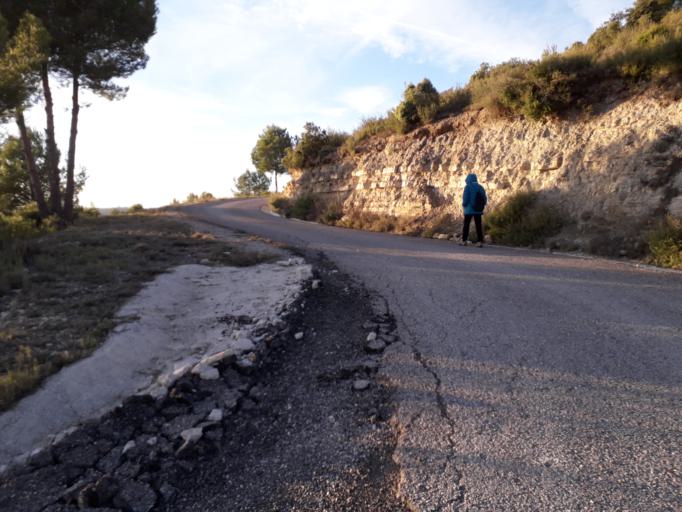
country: ES
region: Catalonia
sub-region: Provincia de Barcelona
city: Jorba
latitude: 41.6228
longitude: 1.5729
